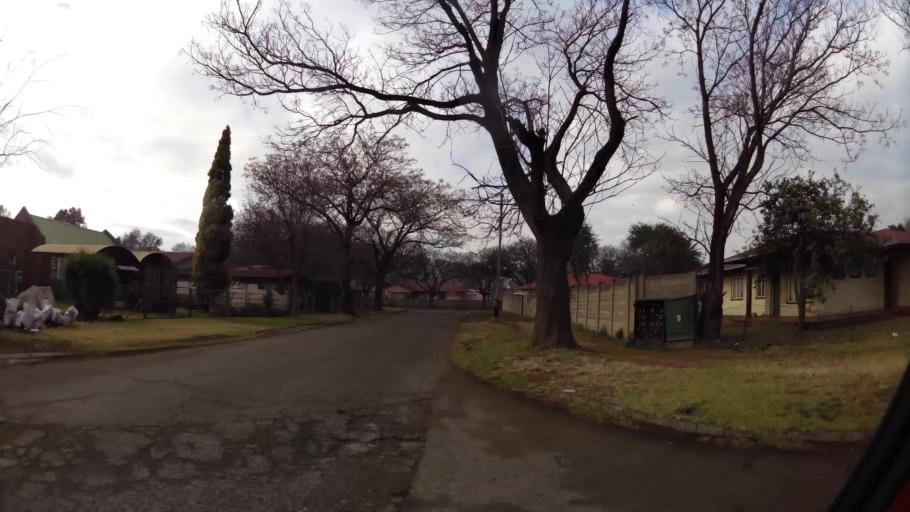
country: ZA
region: Gauteng
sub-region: Sedibeng District Municipality
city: Vanderbijlpark
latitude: -26.6832
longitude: 27.8149
